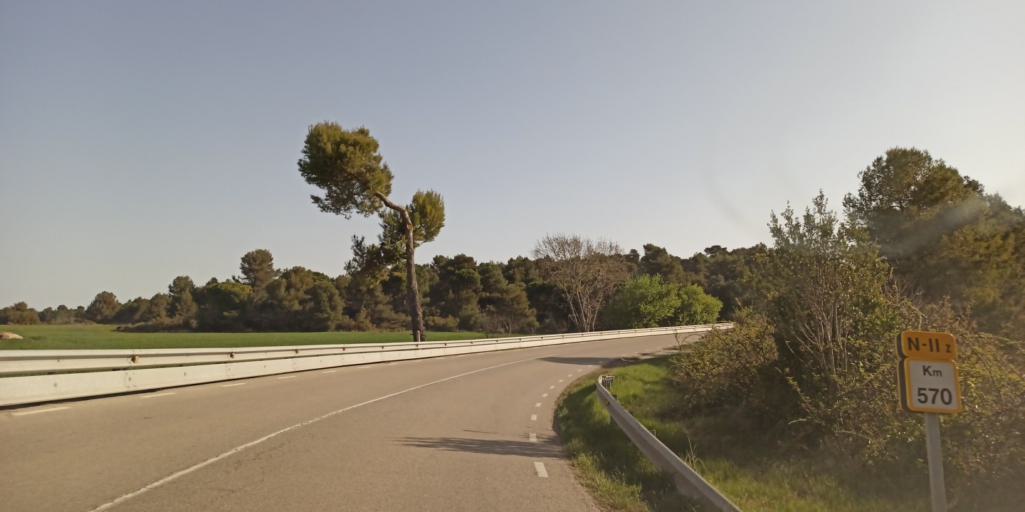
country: ES
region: Catalonia
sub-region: Provincia de Barcelona
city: Castelloli
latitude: 41.5987
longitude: 1.7336
